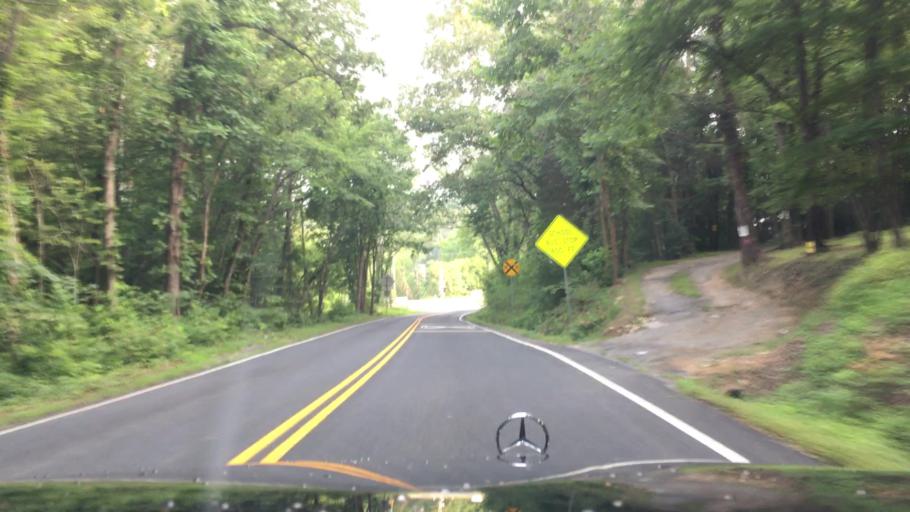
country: US
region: Virginia
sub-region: Campbell County
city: Timberlake
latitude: 37.2337
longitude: -79.2846
